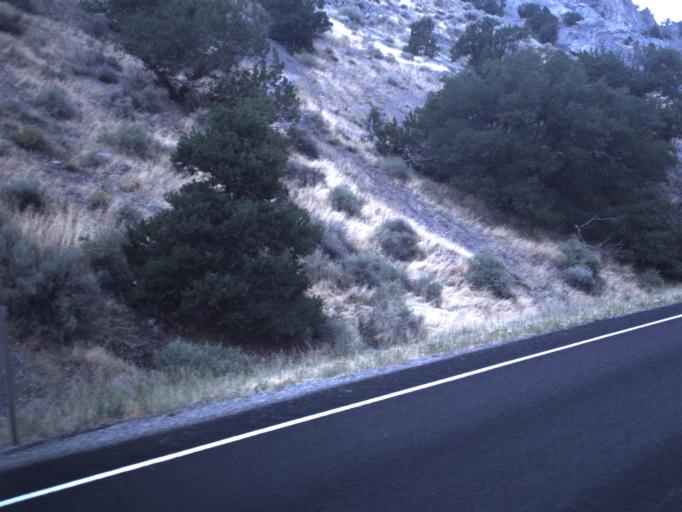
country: US
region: Utah
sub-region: Sevier County
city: Monroe
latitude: 38.5456
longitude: -112.2691
